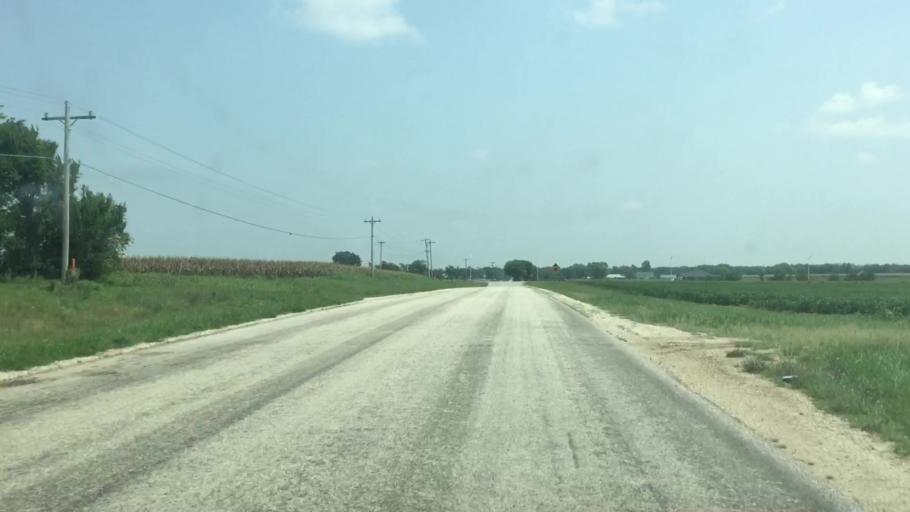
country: US
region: Kansas
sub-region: Allen County
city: Iola
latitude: 37.9512
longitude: -95.3847
